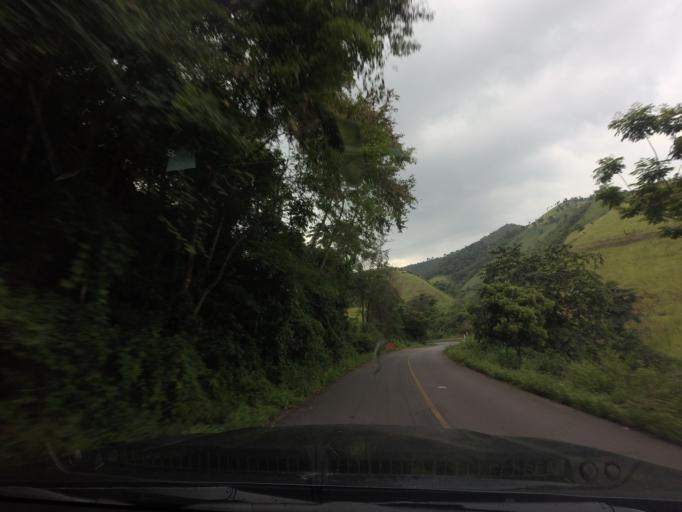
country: TH
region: Nan
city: Bo Kluea
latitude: 19.3376
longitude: 101.1659
